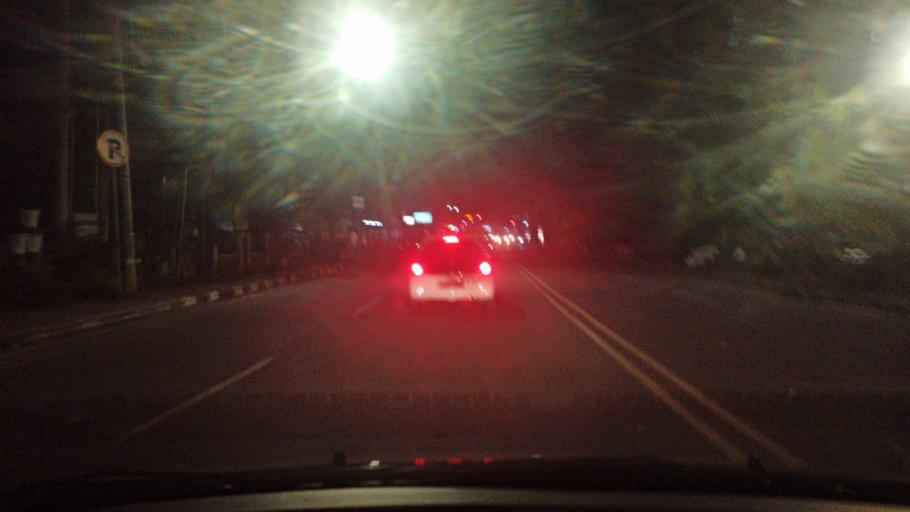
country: ID
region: South Sumatra
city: Palembang
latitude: -2.9891
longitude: 104.7258
